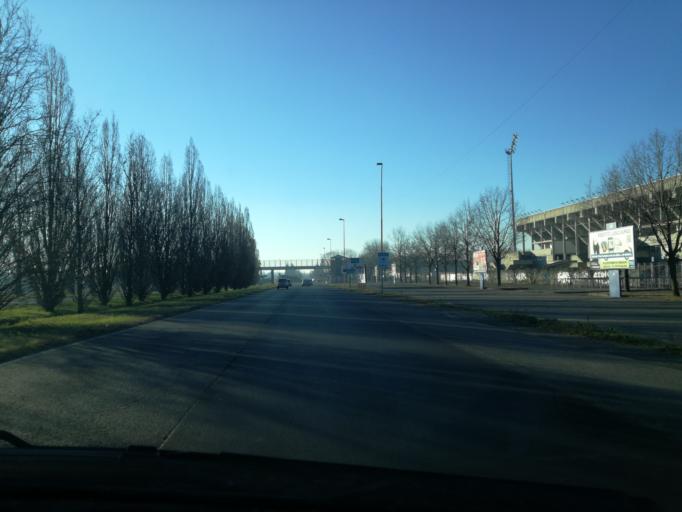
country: IT
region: Lombardy
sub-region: Provincia di Monza e Brianza
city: Villasanta
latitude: 45.5839
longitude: 9.3100
